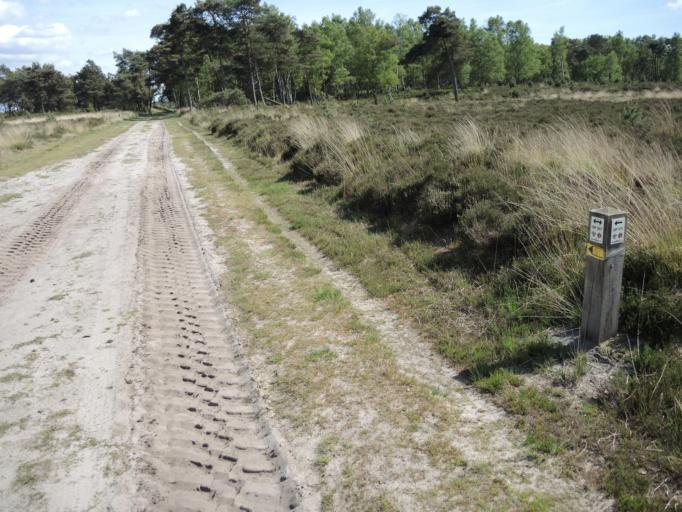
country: BE
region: Flanders
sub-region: Provincie Antwerpen
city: Kalmthout
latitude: 51.3893
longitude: 4.4254
